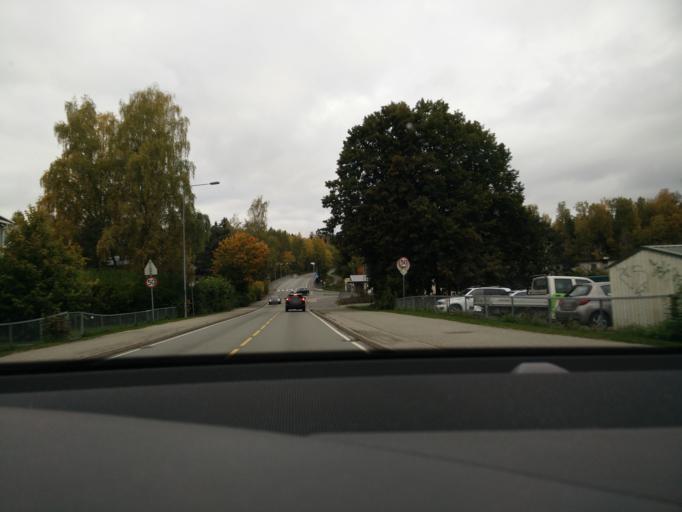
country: NO
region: Akershus
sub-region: Baerum
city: Lysaker
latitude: 59.9361
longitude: 10.6089
